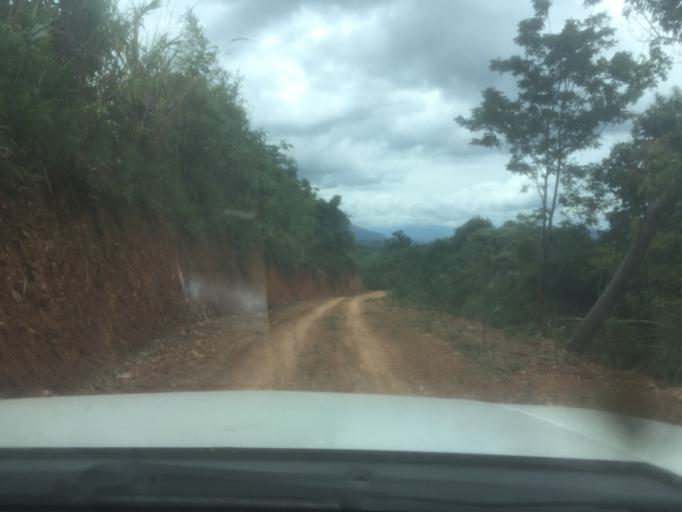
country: LA
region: Phongsali
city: Khoa
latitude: 20.9270
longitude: 102.5371
